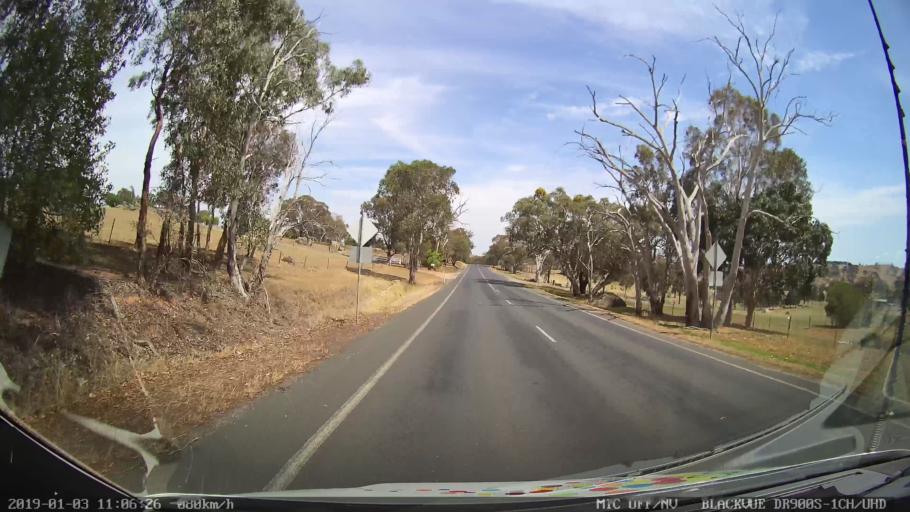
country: AU
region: New South Wales
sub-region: Young
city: Young
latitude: -34.2654
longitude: 148.2731
